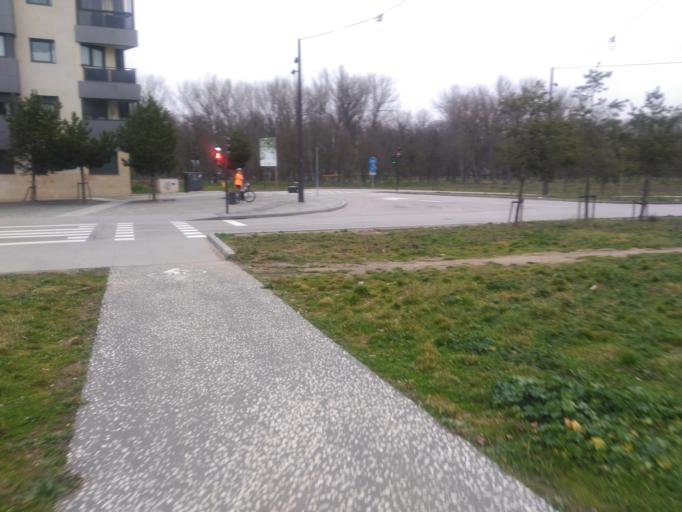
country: ES
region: Castille and Leon
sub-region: Provincia de Burgos
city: Burgos
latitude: 42.3407
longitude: -3.6799
